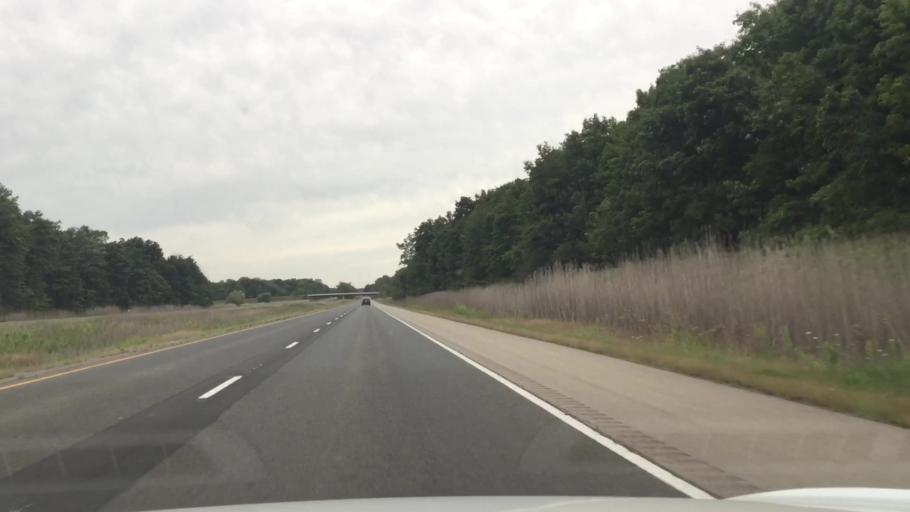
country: CA
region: Ontario
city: Lambton Shores
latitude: 42.9922
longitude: -81.9123
